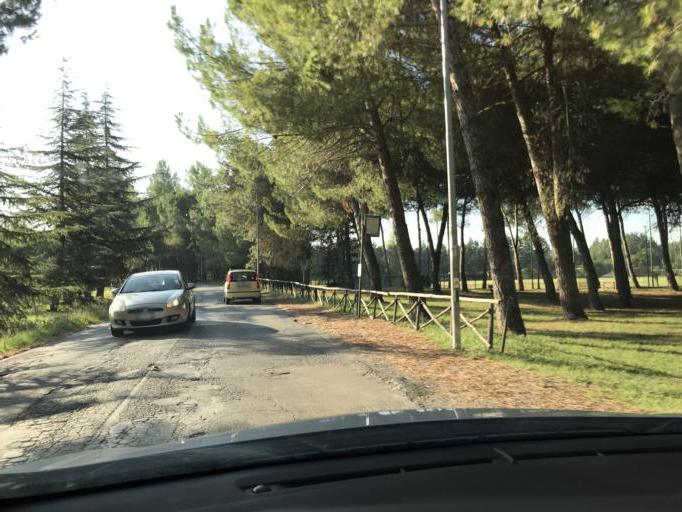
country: IT
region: Umbria
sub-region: Provincia di Perugia
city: Lacugnano
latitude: 43.1155
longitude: 12.3541
